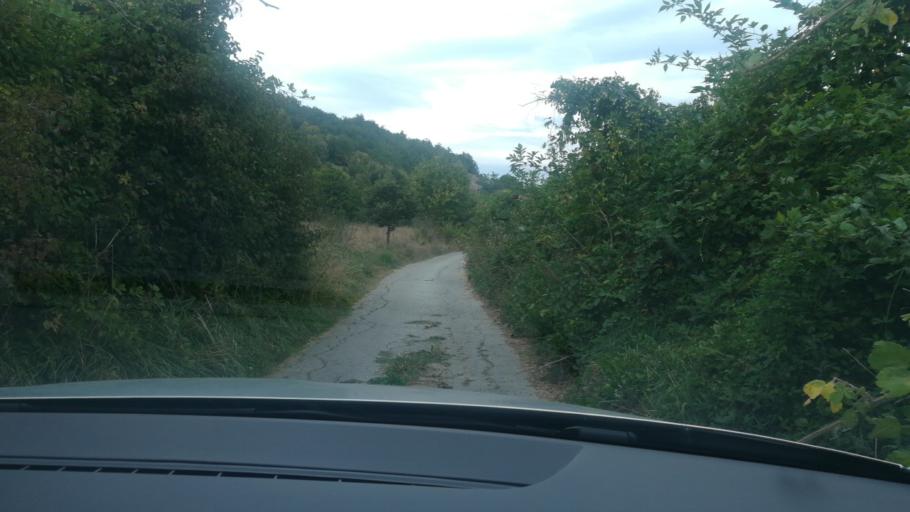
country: MK
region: Debarca
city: Belcista
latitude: 41.2858
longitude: 20.8302
